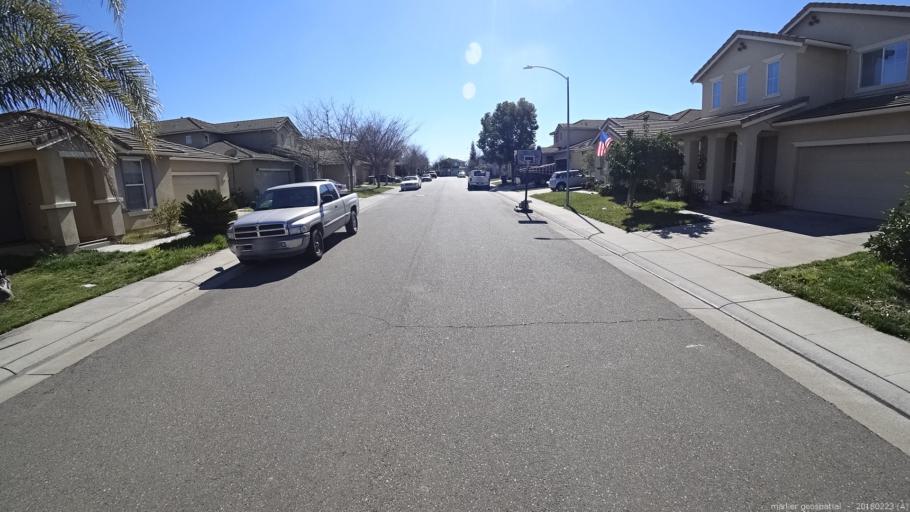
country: US
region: California
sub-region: Sacramento County
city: North Highlands
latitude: 38.7121
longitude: -121.3672
